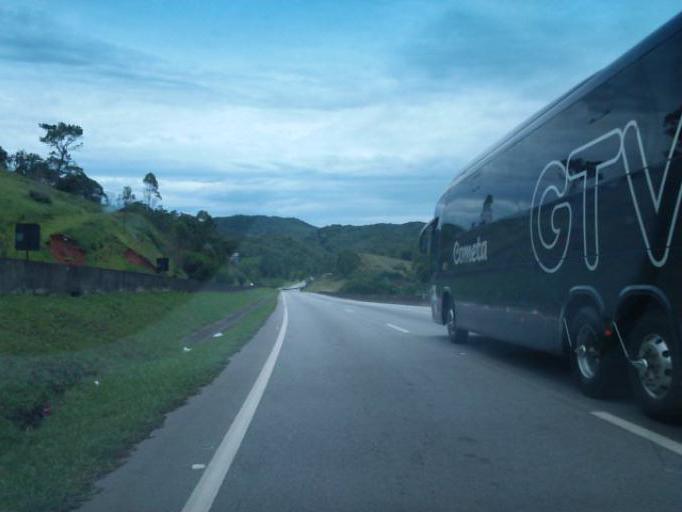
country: BR
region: Sao Paulo
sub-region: Juquitiba
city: Juquitiba
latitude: -24.0120
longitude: -47.1662
